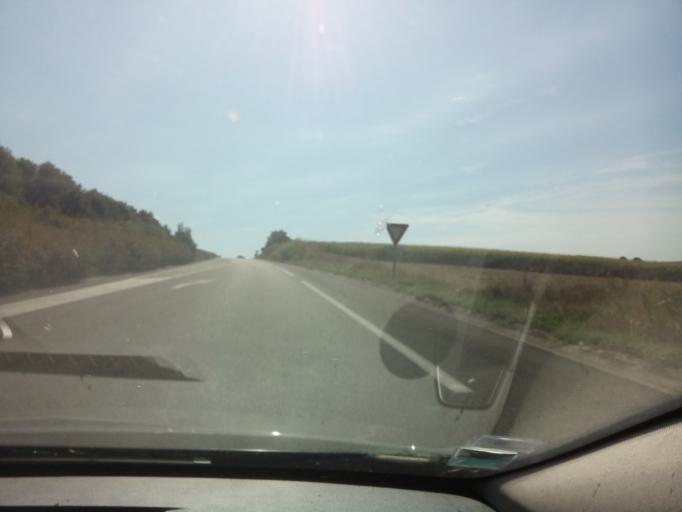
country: FR
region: Alsace
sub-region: Departement du Bas-Rhin
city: Soultz-sous-Forets
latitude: 48.9263
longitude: 7.8976
